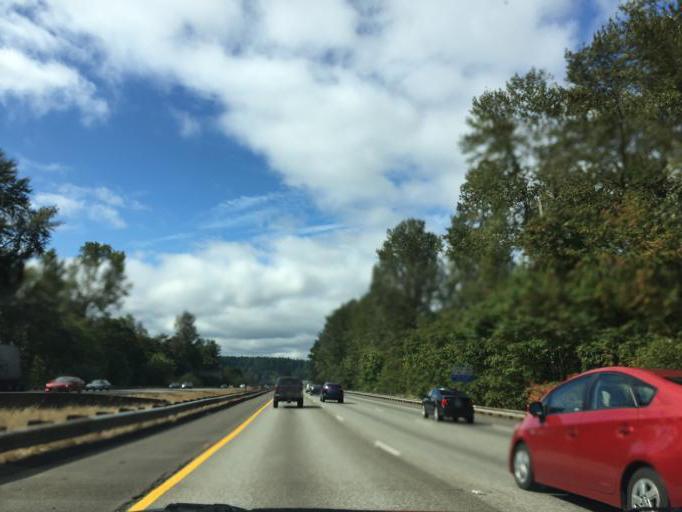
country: US
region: Washington
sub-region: Pierce County
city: DuPont
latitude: 47.0714
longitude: -122.7053
